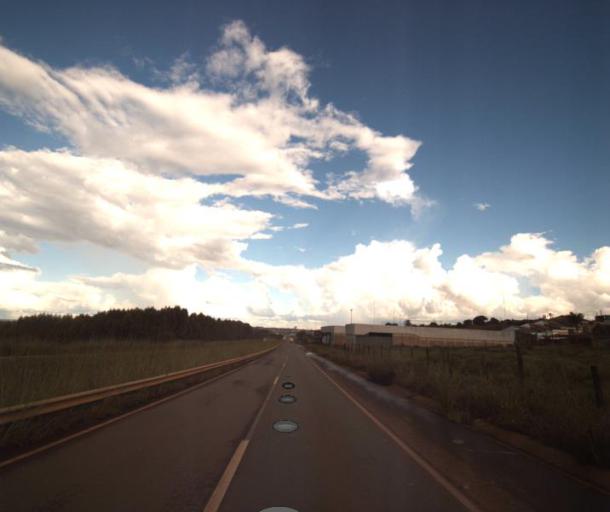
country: BR
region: Goias
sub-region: Anapolis
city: Anapolis
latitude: -16.2604
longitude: -48.9865
